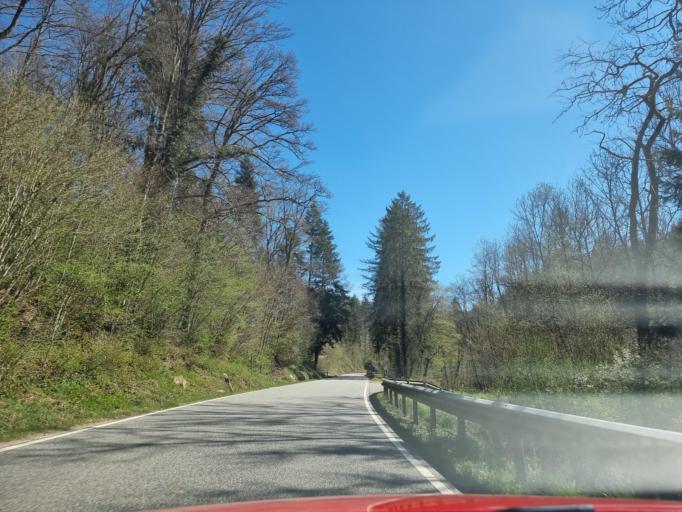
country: DE
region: Rheinland-Pfalz
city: Kordel
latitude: 49.8528
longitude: 6.6041
